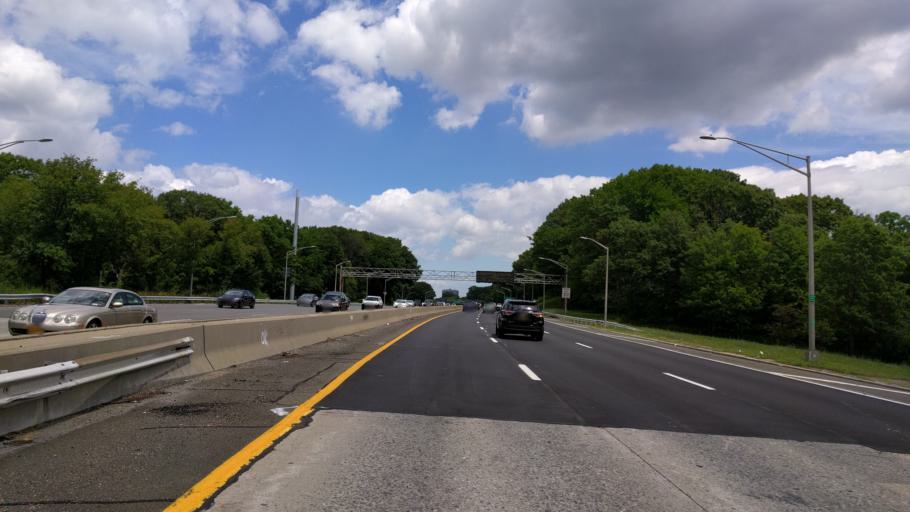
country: US
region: New York
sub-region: Nassau County
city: Bellerose Terrace
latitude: 40.7326
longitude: -73.7465
